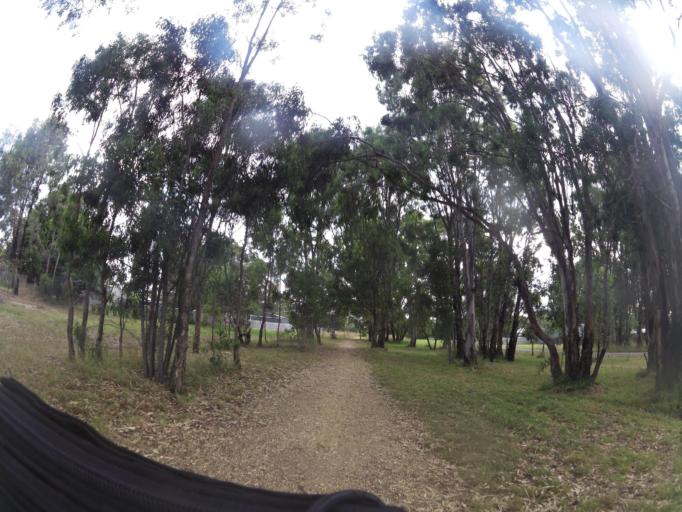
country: AU
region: Victoria
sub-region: Latrobe
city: Traralgon
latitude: -38.0585
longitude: 146.6269
